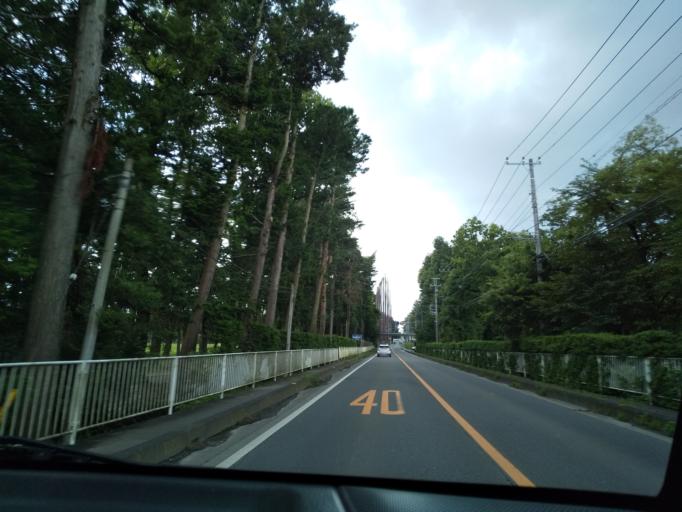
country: JP
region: Saitama
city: Hanno
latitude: 35.8619
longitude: 139.3615
